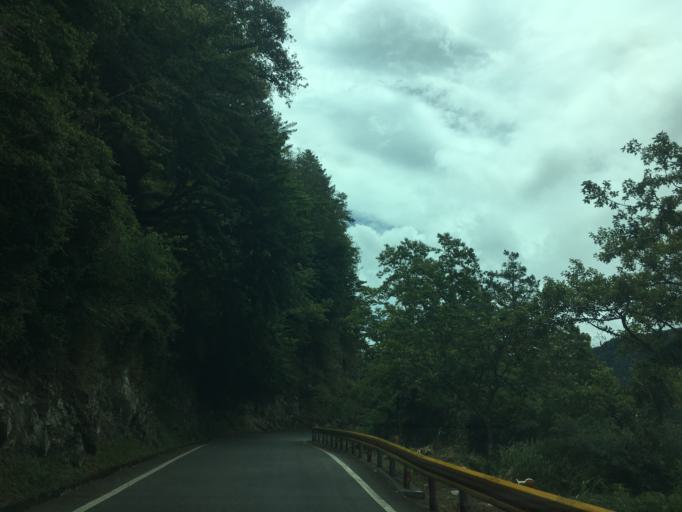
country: TW
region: Taiwan
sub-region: Hualien
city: Hualian
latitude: 24.1825
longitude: 121.3548
